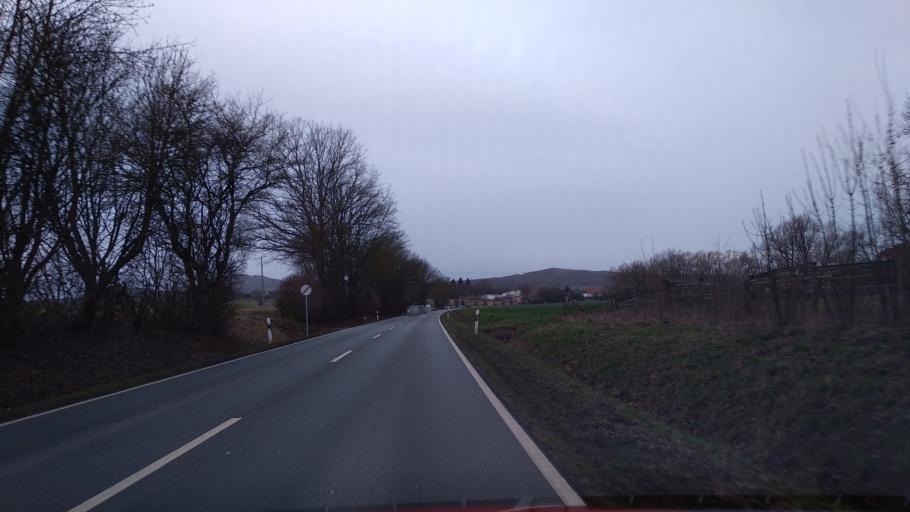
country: DE
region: Hesse
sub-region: Regierungsbezirk Kassel
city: Calden
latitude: 51.3671
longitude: 9.4108
